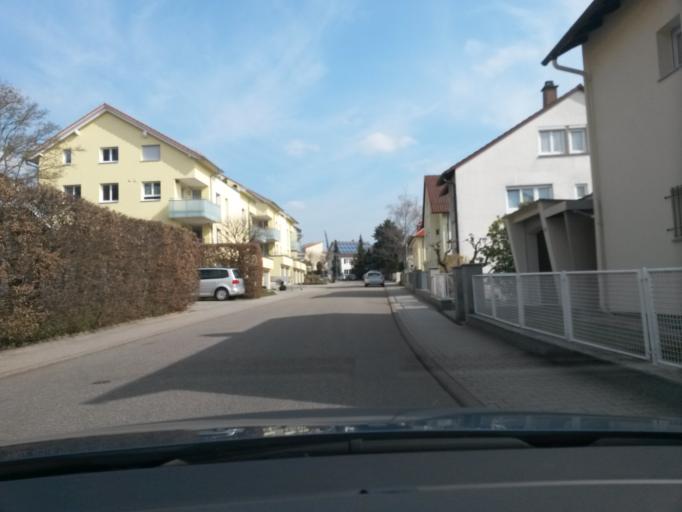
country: DE
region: Baden-Wuerttemberg
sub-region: Karlsruhe Region
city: Pforzheim
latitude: 48.9008
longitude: 8.7124
